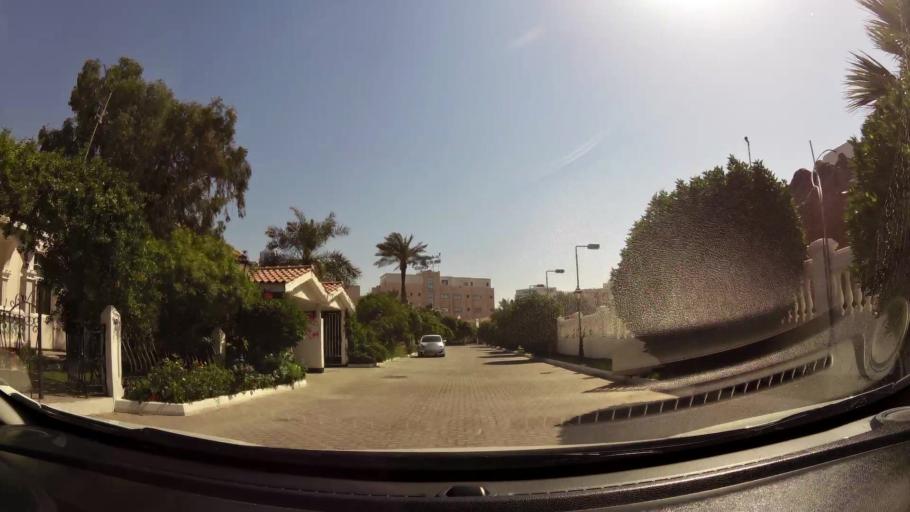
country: BH
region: Manama
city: Manama
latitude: 26.2093
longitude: 50.5769
